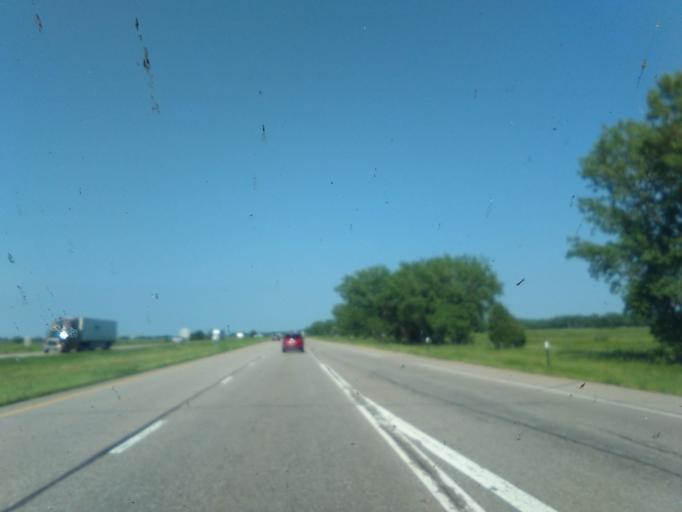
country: US
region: Nebraska
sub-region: Hall County
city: Wood River
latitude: 40.7636
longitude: -98.5847
